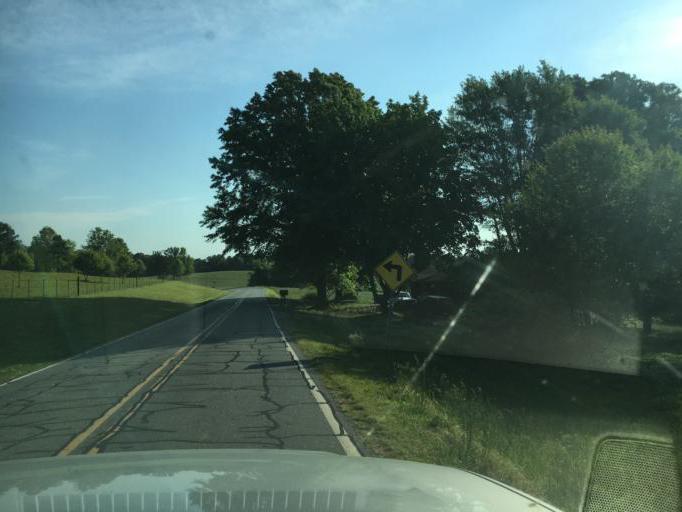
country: US
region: North Carolina
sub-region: Rutherford County
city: Rutherfordton
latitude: 35.3488
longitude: -81.9858
